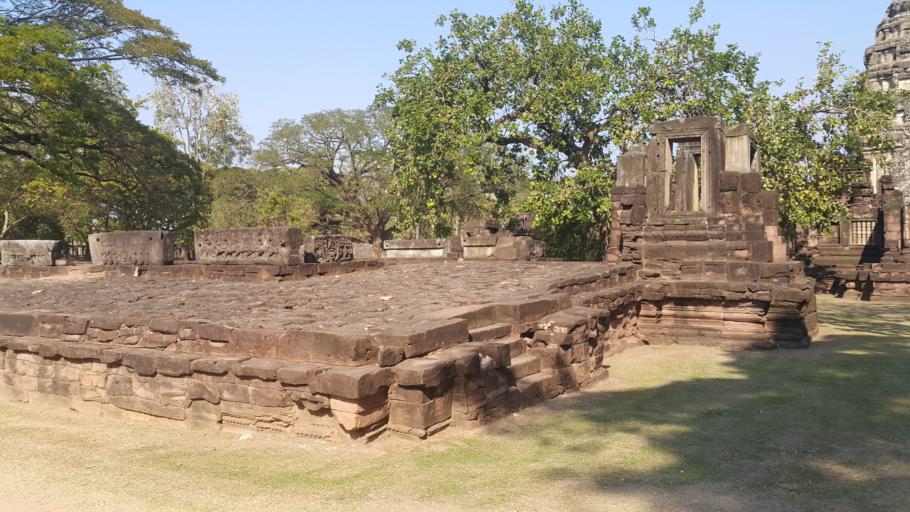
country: TH
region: Nakhon Ratchasima
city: Phimai
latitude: 15.2208
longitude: 102.4931
